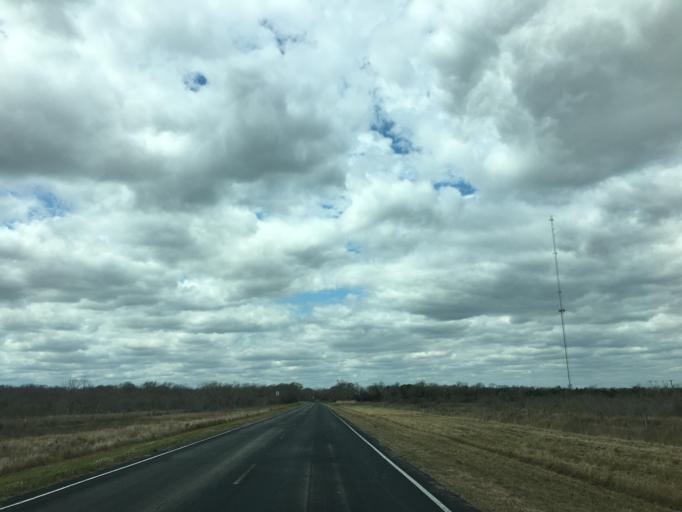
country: US
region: Texas
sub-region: Brazoria County
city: Oyster Creek
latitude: 29.0653
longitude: -95.3144
